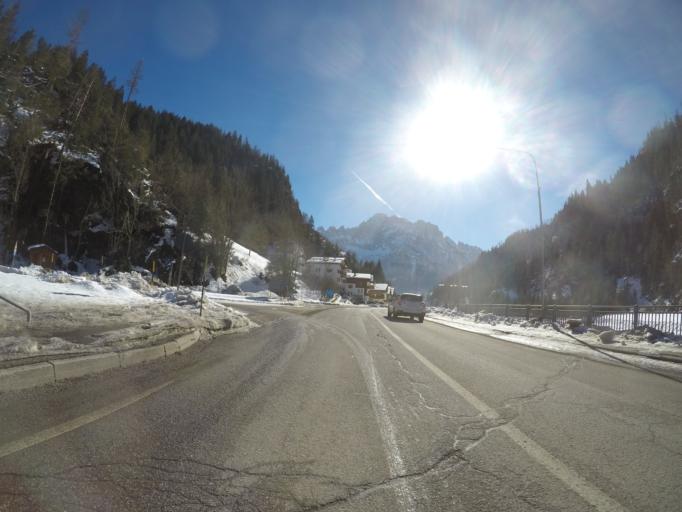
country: IT
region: Veneto
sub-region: Provincia di Belluno
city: Rocca Pietore
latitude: 46.4355
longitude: 11.9963
